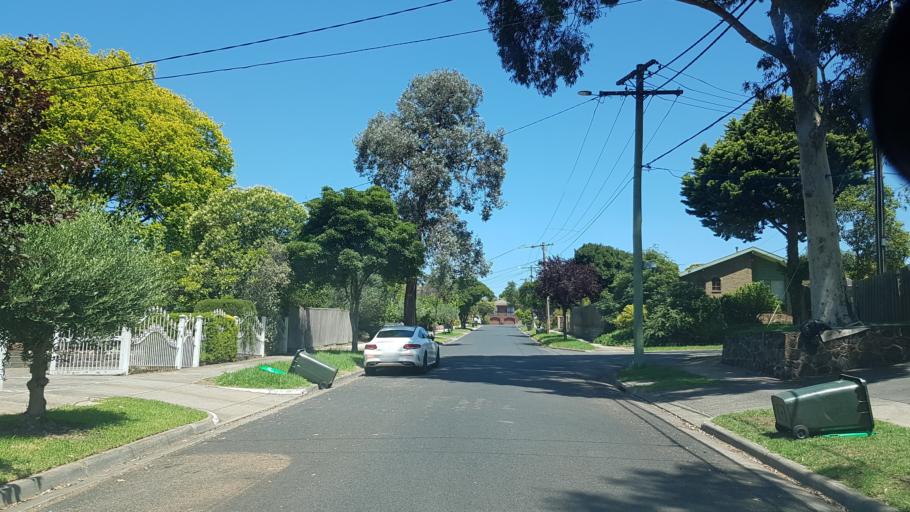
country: AU
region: Victoria
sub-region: Banyule
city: Viewbank
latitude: -37.7564
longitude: 145.0987
